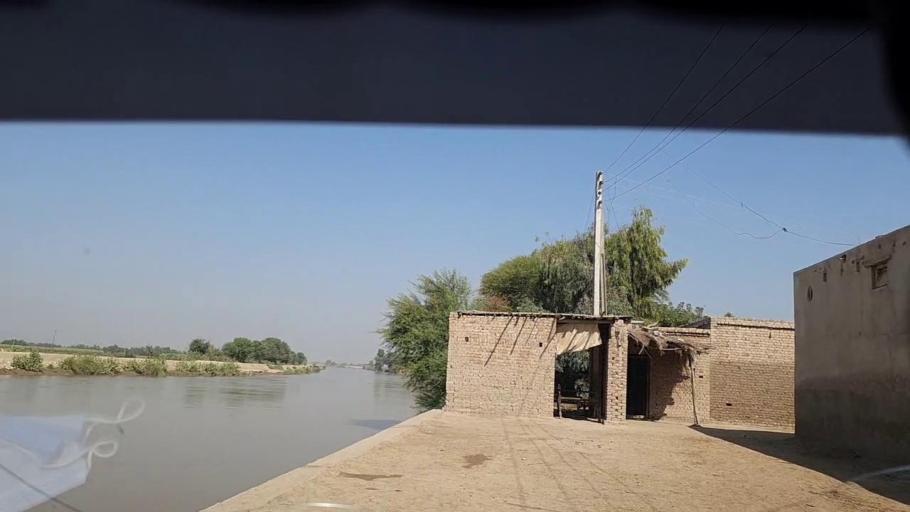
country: PK
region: Sindh
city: Naudero
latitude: 27.6690
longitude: 68.3783
